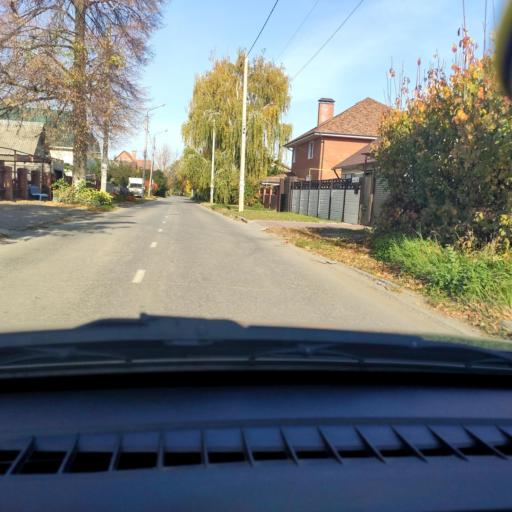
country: RU
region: Samara
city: Tol'yatti
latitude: 53.5223
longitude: 49.4081
